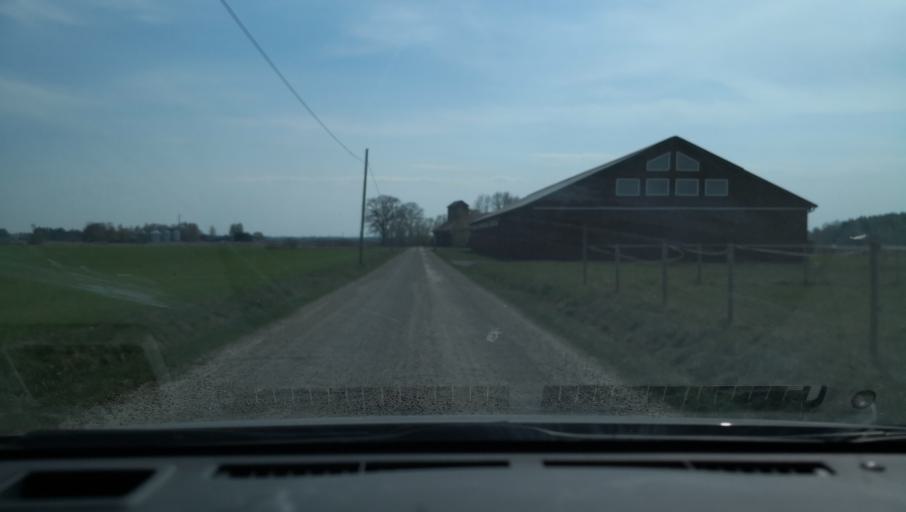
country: SE
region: Vaestmanland
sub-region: Vasteras
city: Skultuna
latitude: 59.7987
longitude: 16.4361
